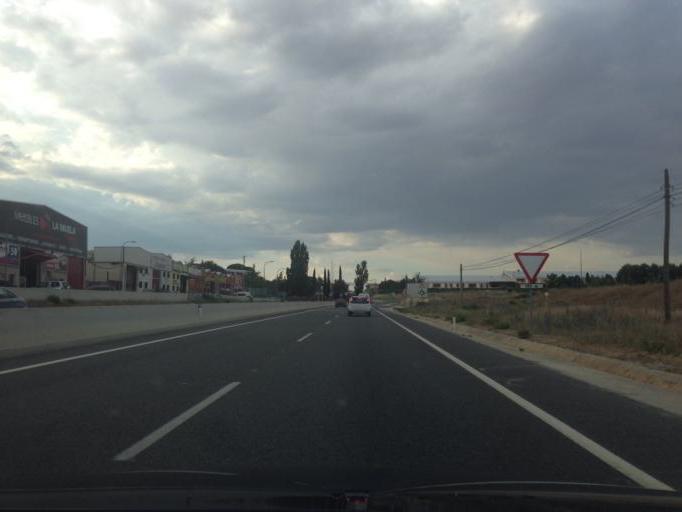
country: ES
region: Madrid
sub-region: Provincia de Madrid
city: Ajalvir
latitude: 40.5015
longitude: -3.4794
